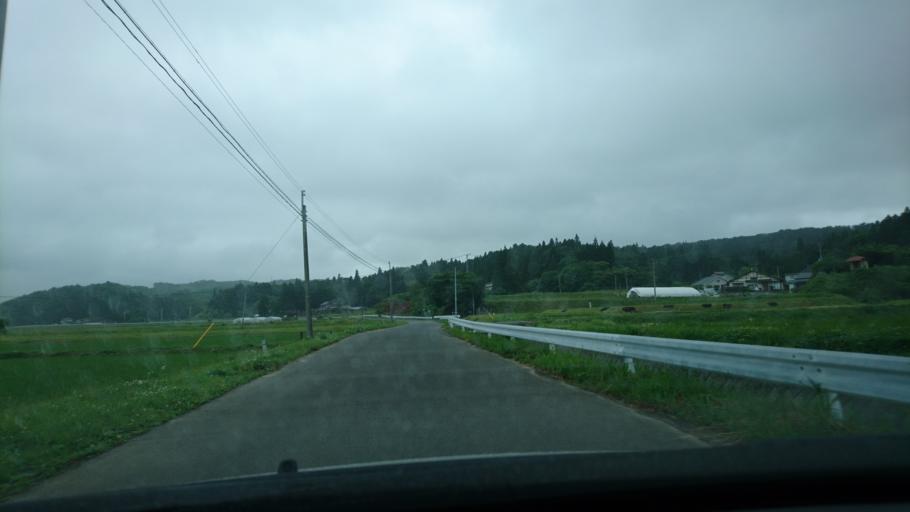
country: JP
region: Iwate
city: Ichinoseki
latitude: 38.9509
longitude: 141.0484
